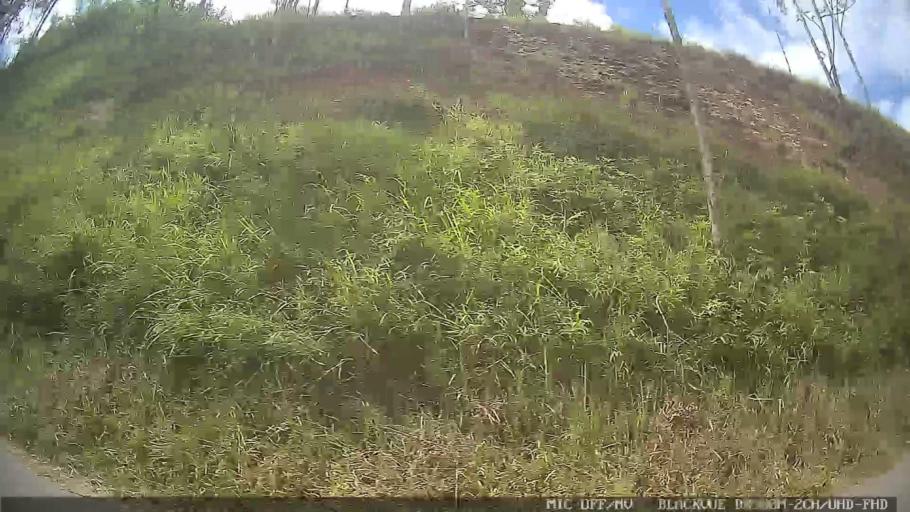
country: BR
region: Sao Paulo
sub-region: Braganca Paulista
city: Braganca Paulista
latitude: -22.8016
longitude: -46.5159
